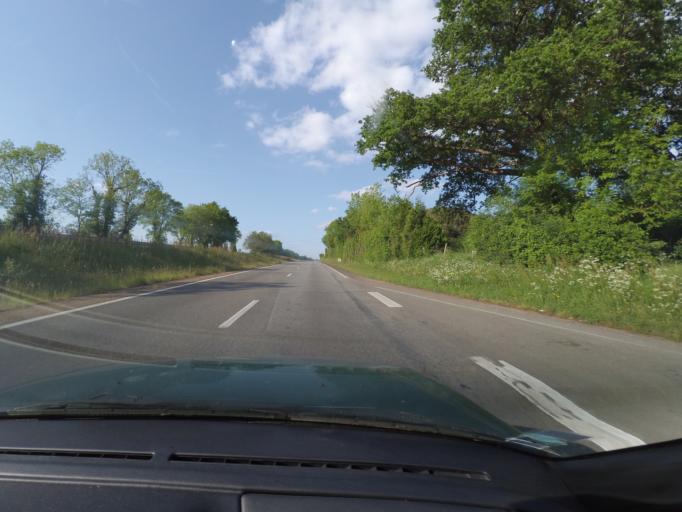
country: FR
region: Pays de la Loire
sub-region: Departement de la Vendee
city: Saligny
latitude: 46.8281
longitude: -1.4268
